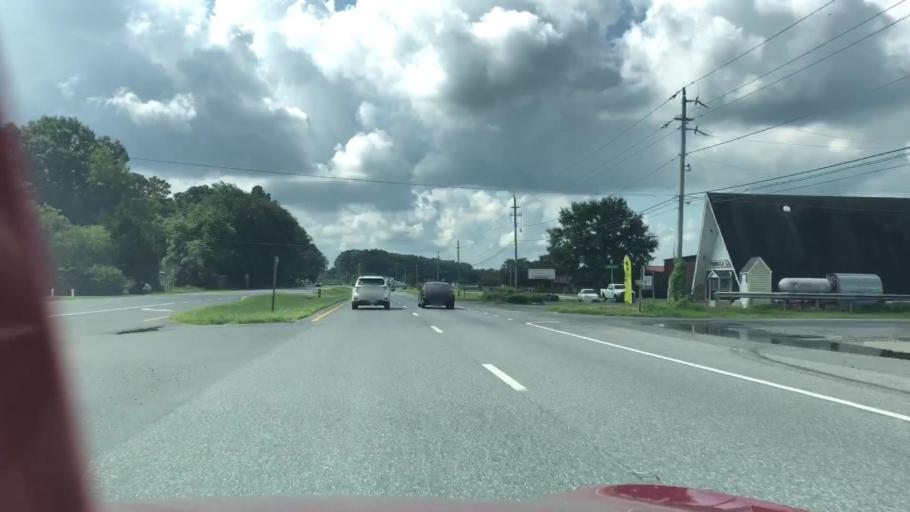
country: US
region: Virginia
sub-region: Accomack County
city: Wattsville
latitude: 37.9270
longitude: -75.5488
